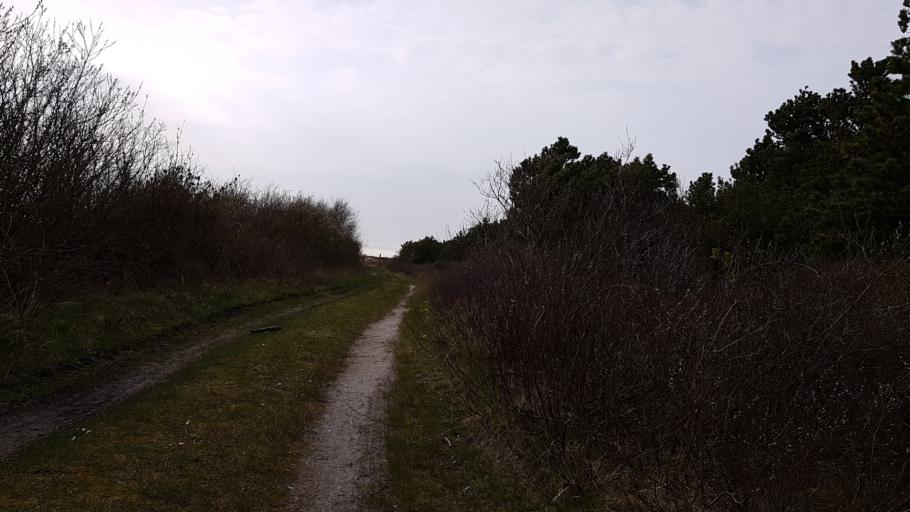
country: DE
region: Schleswig-Holstein
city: List
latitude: 55.1650
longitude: 8.5308
